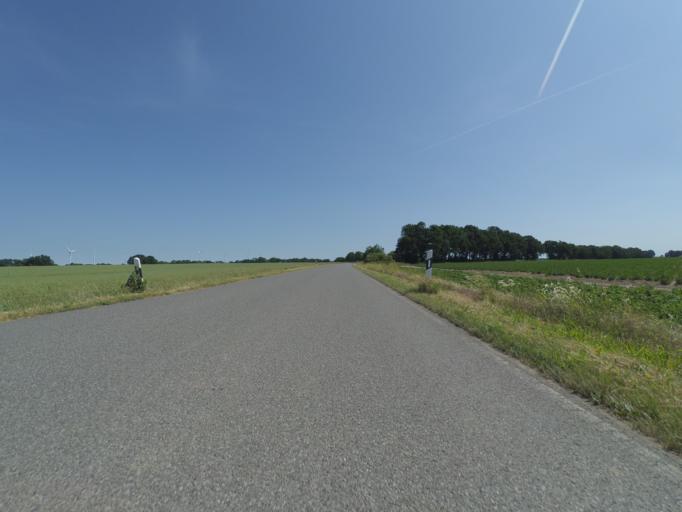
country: DE
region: Brandenburg
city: Heiligengrabe
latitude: 53.1607
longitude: 12.2740
